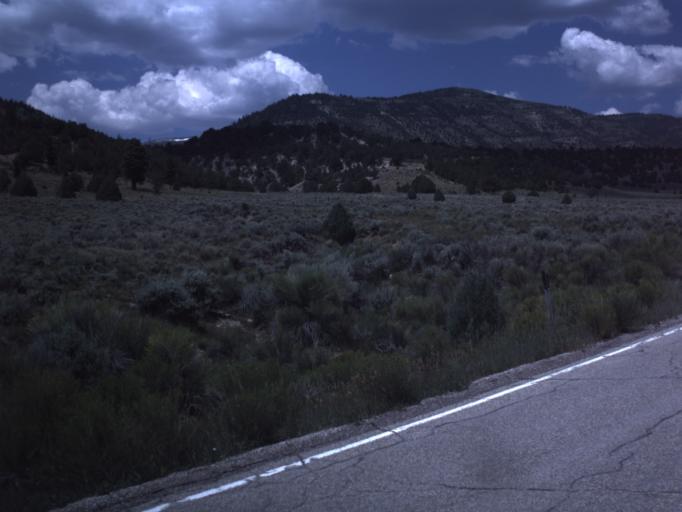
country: US
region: Utah
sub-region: Emery County
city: Orangeville
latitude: 39.3183
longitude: -111.2827
